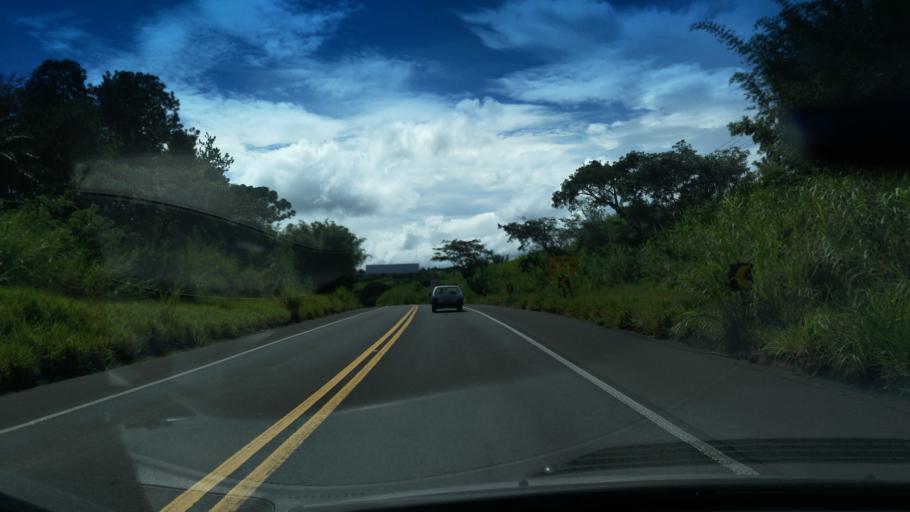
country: BR
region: Sao Paulo
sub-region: Santo Antonio Do Jardim
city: Espirito Santo do Pinhal
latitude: -22.1610
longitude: -46.7308
